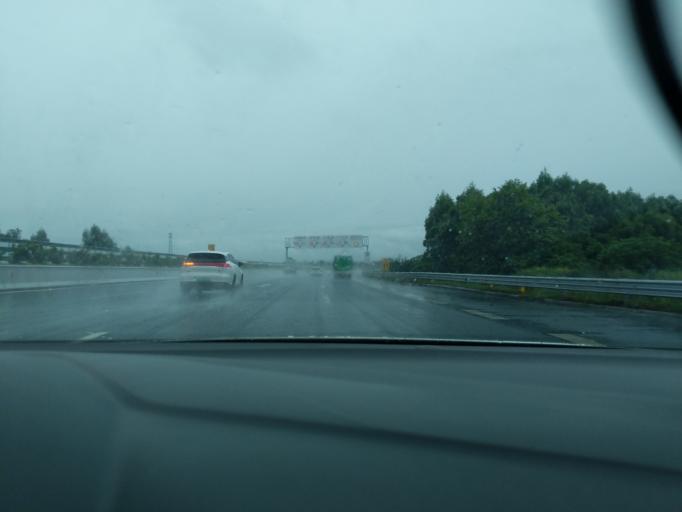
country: CN
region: Guangdong
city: Shuikou
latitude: 22.4832
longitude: 112.7770
